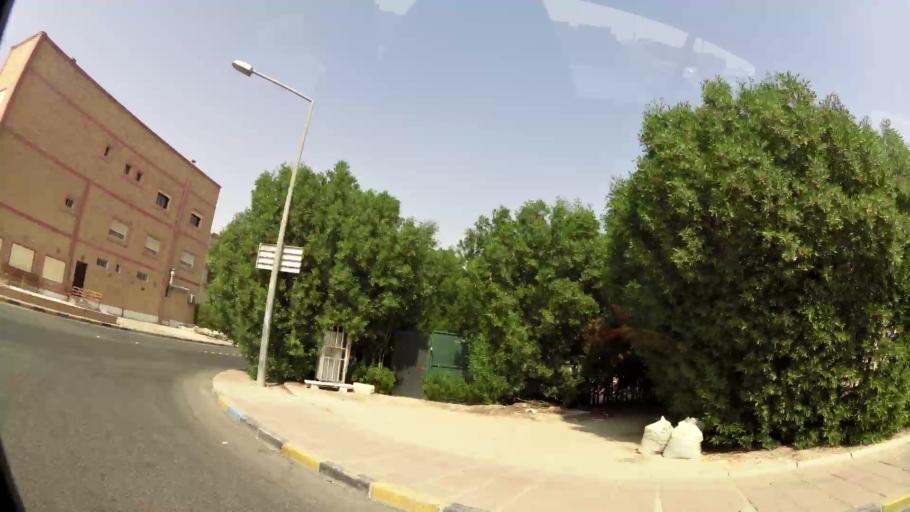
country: KW
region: Muhafazat al Jahra'
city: Al Jahra'
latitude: 29.3256
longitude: 47.6634
